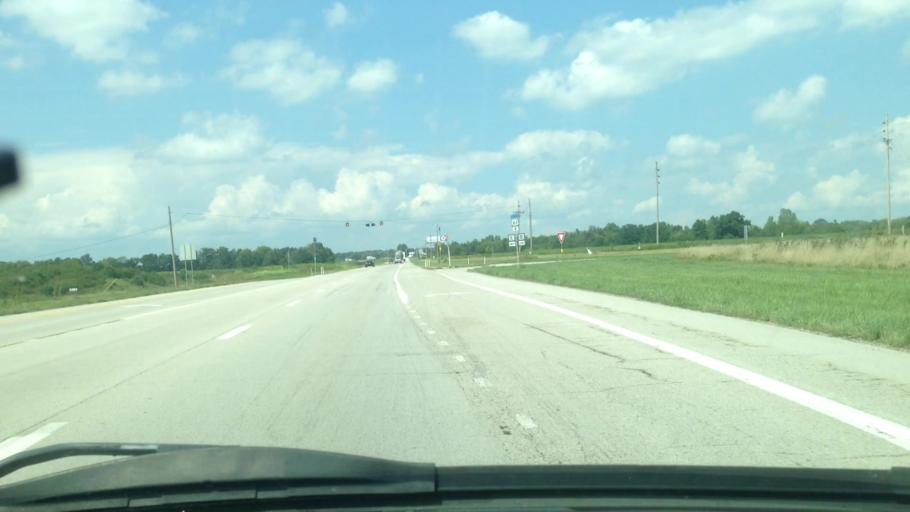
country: US
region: Missouri
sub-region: Lincoln County
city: Troy
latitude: 39.1270
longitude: -90.9638
